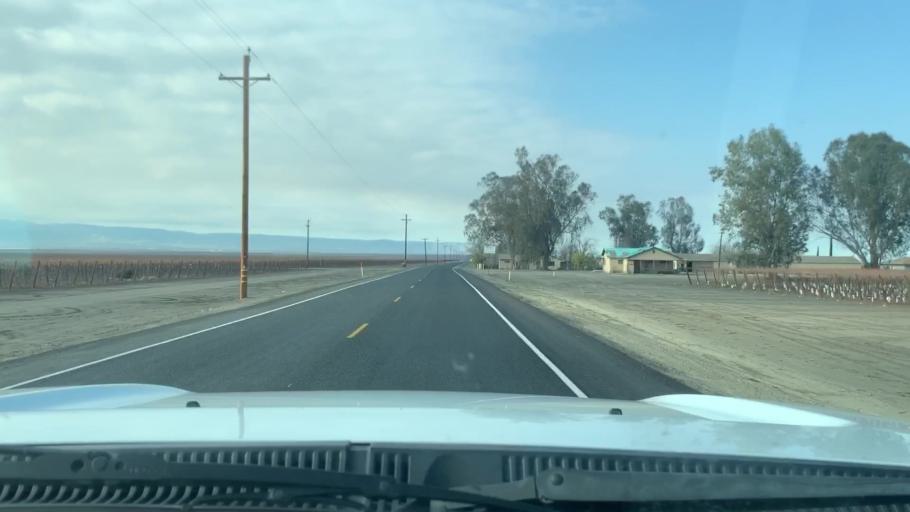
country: US
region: California
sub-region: Kern County
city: Buttonwillow
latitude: 35.4994
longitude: -119.5802
